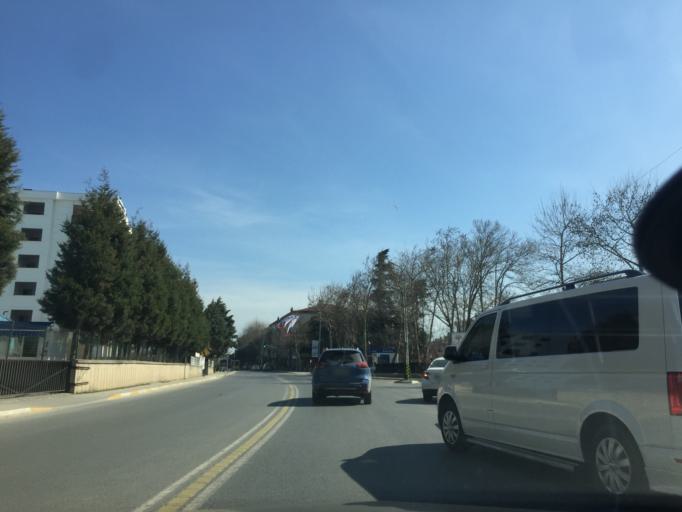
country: TR
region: Istanbul
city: Icmeler
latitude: 40.8308
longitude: 29.3184
